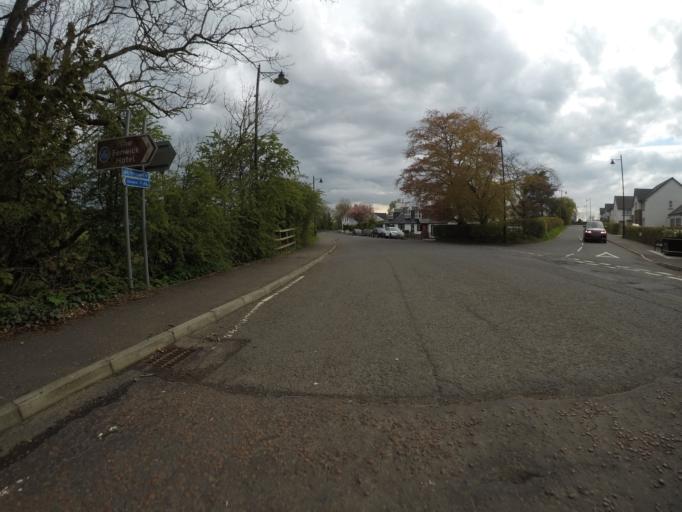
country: GB
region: Scotland
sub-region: East Ayrshire
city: Kilmarnock
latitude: 55.6535
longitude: -4.4474
